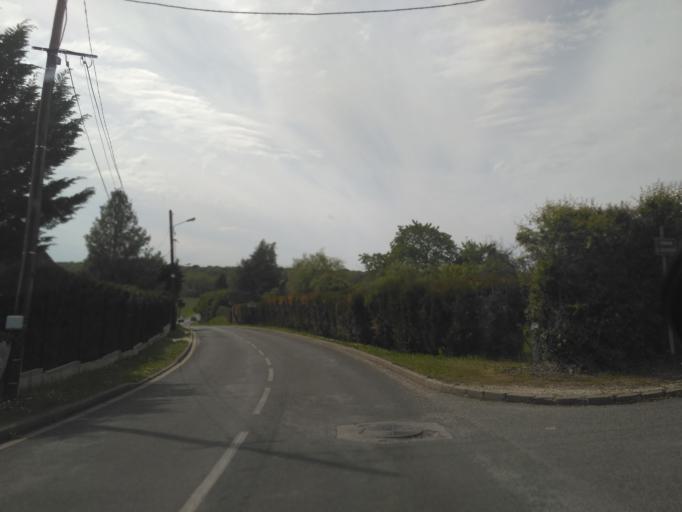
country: FR
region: Ile-de-France
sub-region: Departement de Seine-et-Marne
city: Chaumes-en-Brie
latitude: 48.6659
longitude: 2.8304
